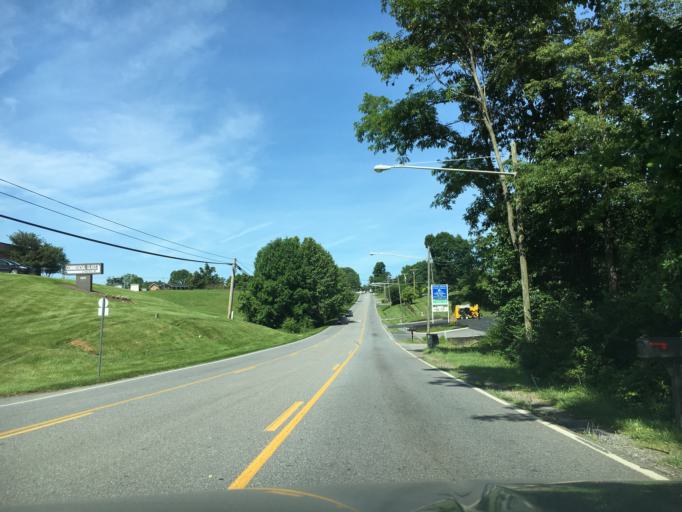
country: US
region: Virginia
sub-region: City of Lynchburg
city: West Lynchburg
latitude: 37.3992
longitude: -79.2101
